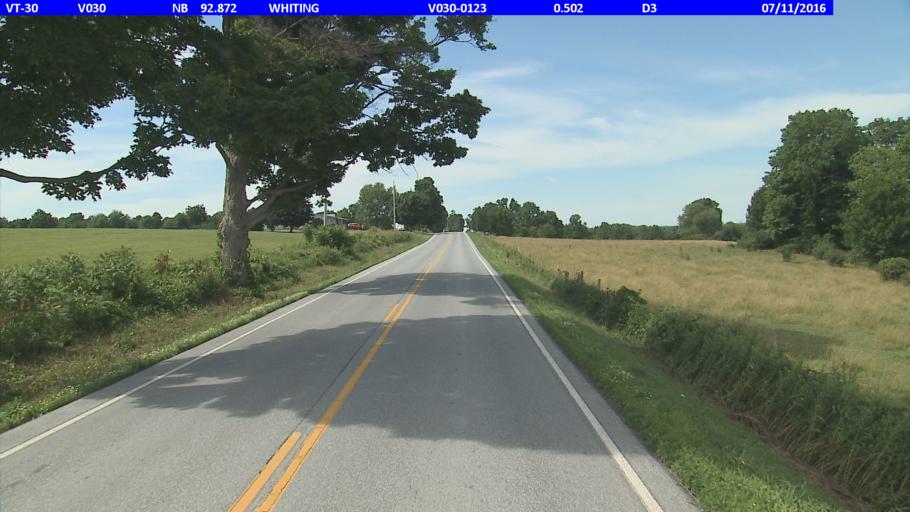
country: US
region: Vermont
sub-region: Rutland County
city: Brandon
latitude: 43.8453
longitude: -73.1968
